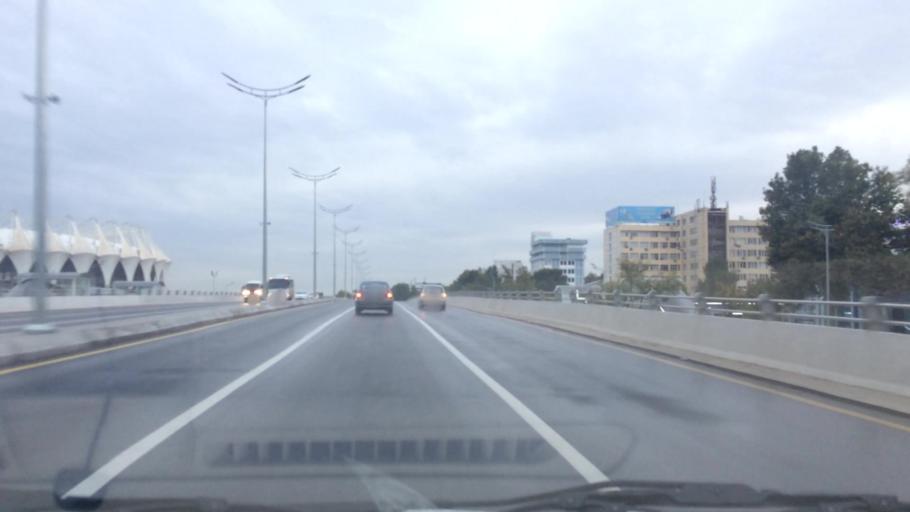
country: UZ
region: Toshkent Shahri
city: Tashkent
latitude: 41.2831
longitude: 69.2136
